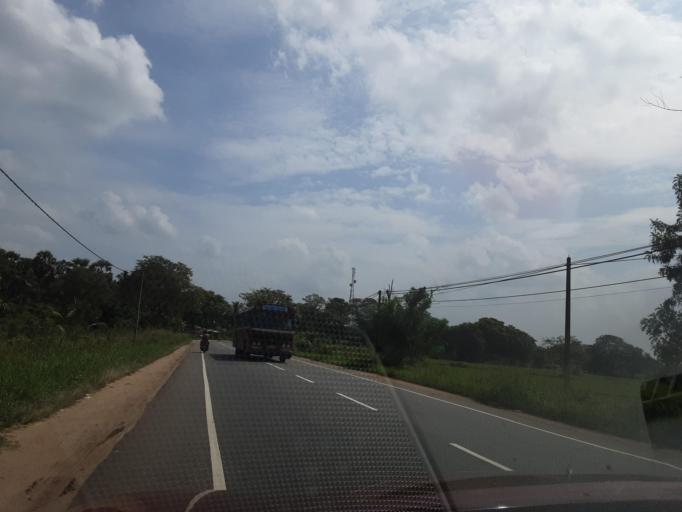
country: LK
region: Northern Province
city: Vavuniya
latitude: 8.5320
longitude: 80.4972
